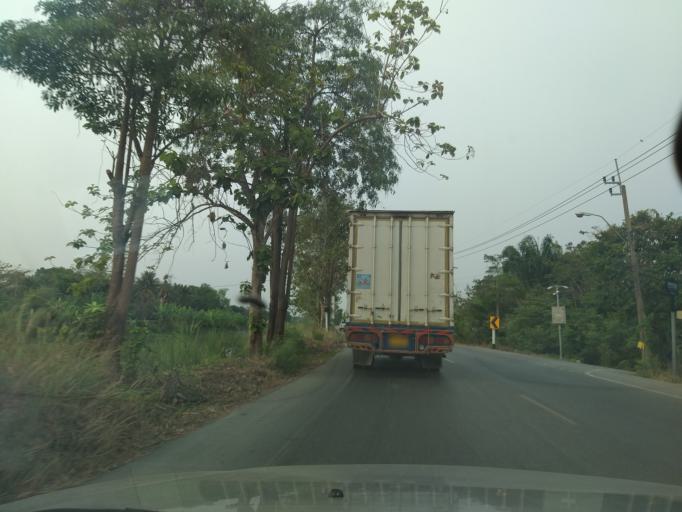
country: TH
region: Bangkok
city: Nong Chok
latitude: 13.8781
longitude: 100.8848
